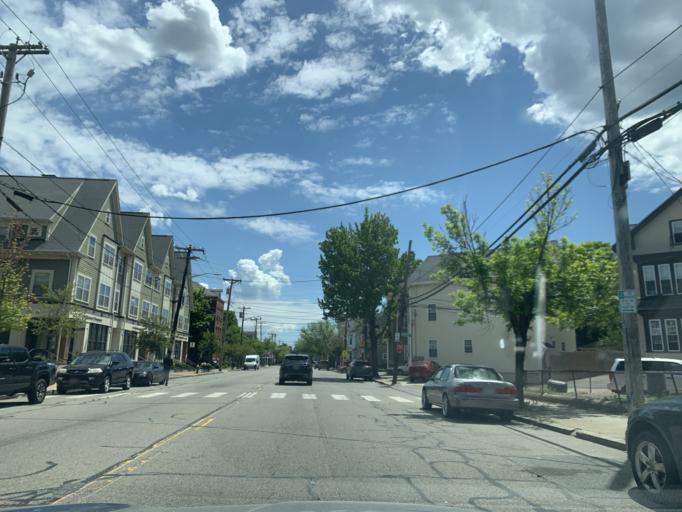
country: US
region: Rhode Island
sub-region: Providence County
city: Providence
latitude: 41.8378
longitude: -71.4239
